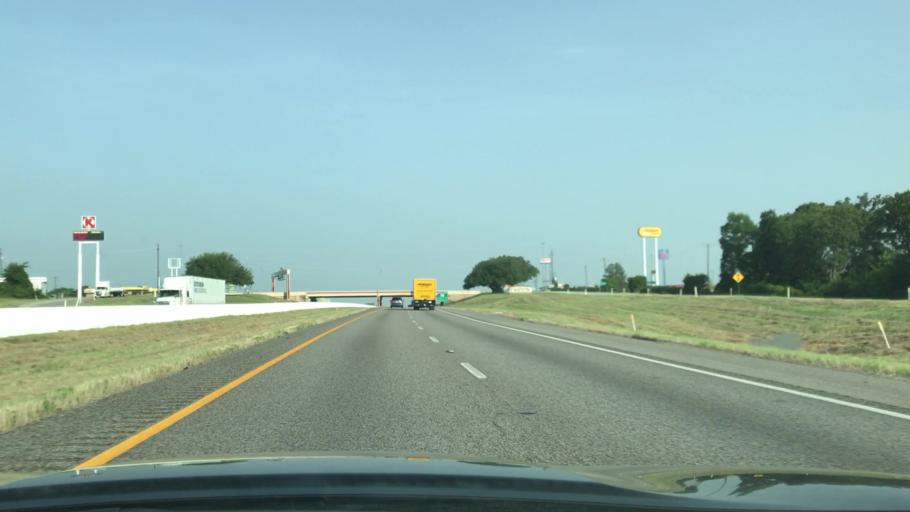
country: US
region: Texas
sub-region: Van Zandt County
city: Canton
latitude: 32.5771
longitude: -95.8515
